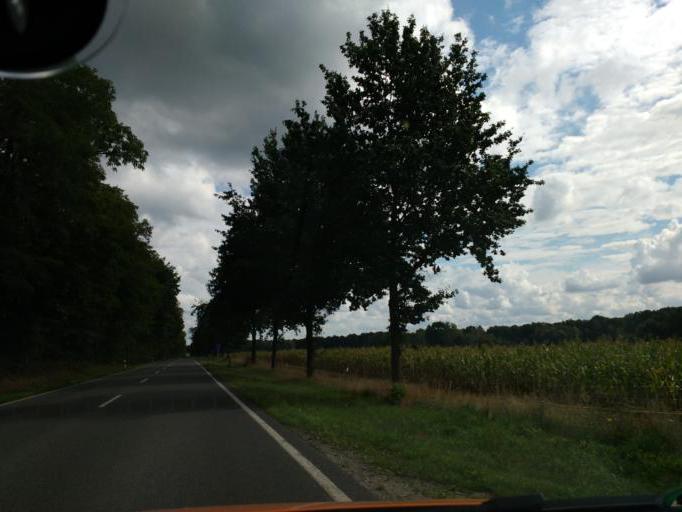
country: DE
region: Brandenburg
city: Marienwerder
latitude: 52.8534
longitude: 13.5696
